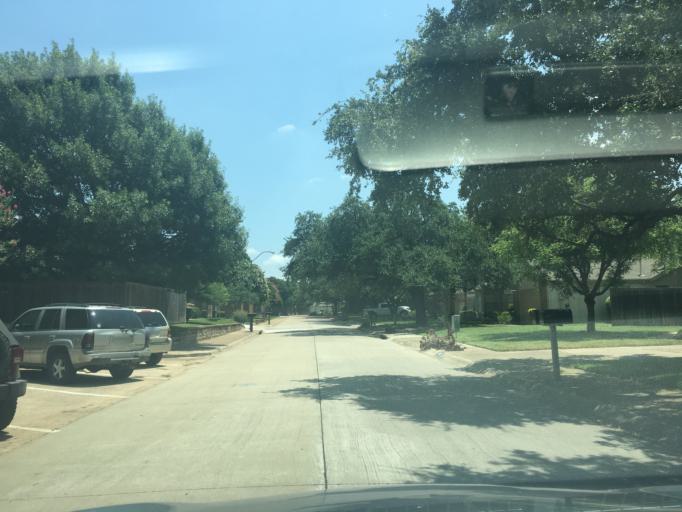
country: US
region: Texas
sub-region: Dallas County
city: Addison
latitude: 32.9205
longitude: -96.8468
